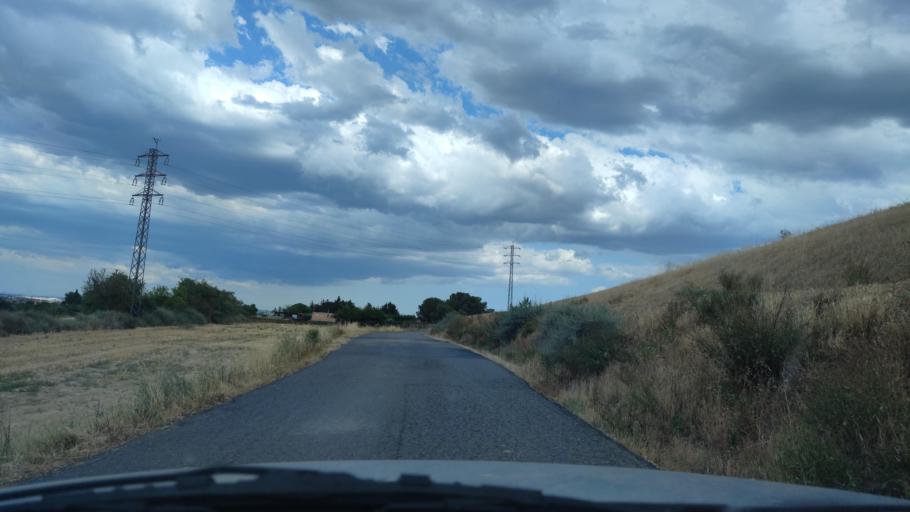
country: ES
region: Catalonia
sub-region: Provincia de Lleida
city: Lleida
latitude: 41.6165
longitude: 0.5757
